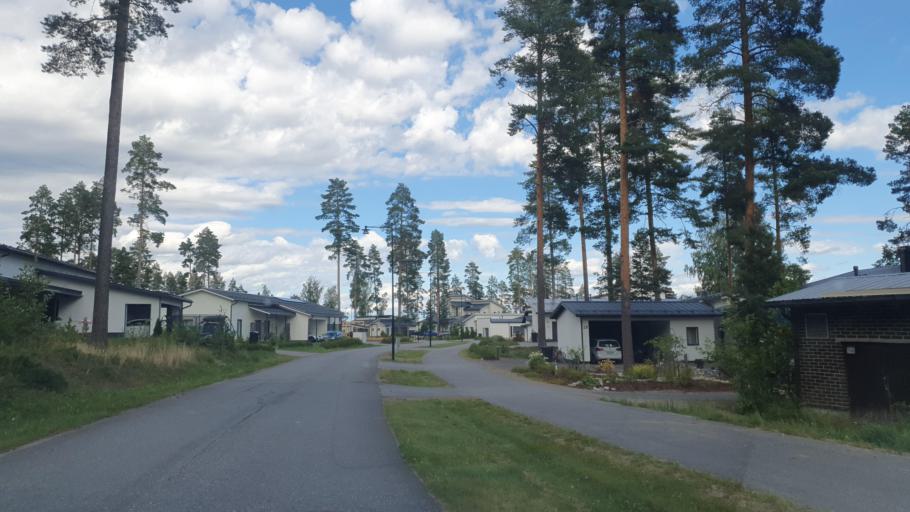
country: FI
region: Central Finland
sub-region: Jyvaeskylae
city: Saeynaetsalo
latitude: 62.1610
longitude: 25.7670
